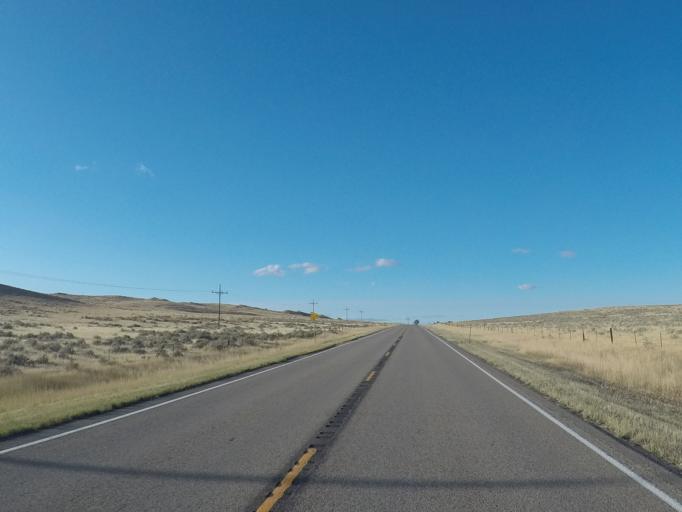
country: US
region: Montana
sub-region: Golden Valley County
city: Ryegate
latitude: 46.2372
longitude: -108.9346
